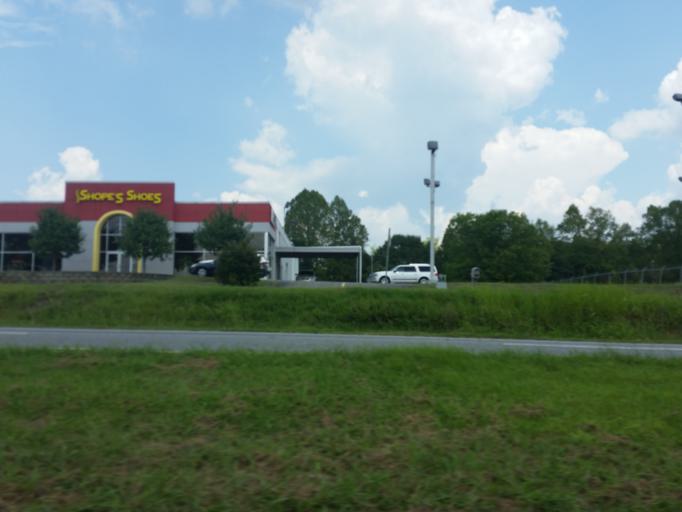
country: US
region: North Carolina
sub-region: Cleveland County
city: Shelby
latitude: 35.2700
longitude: -81.4911
